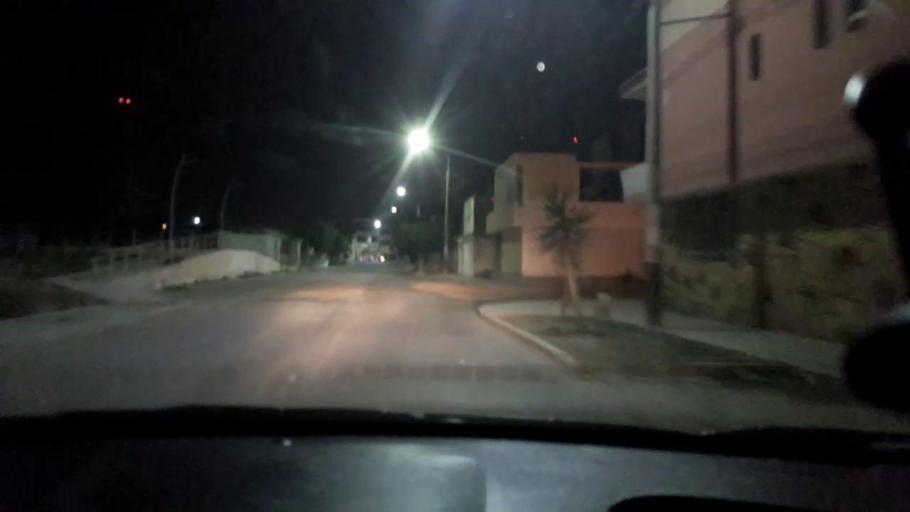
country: PE
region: Lambayeque
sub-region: Provincia de Chiclayo
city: Chiclayo
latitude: -6.7867
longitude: -79.8415
